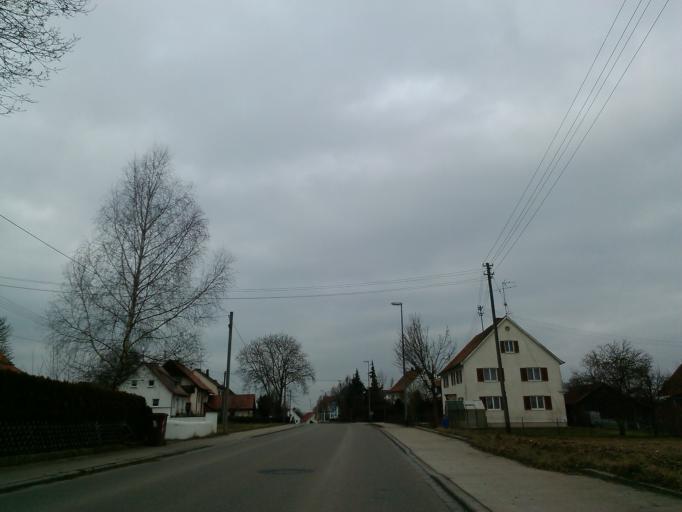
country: DE
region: Bavaria
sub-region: Swabia
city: Langenneufnach
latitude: 48.3057
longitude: 10.6081
